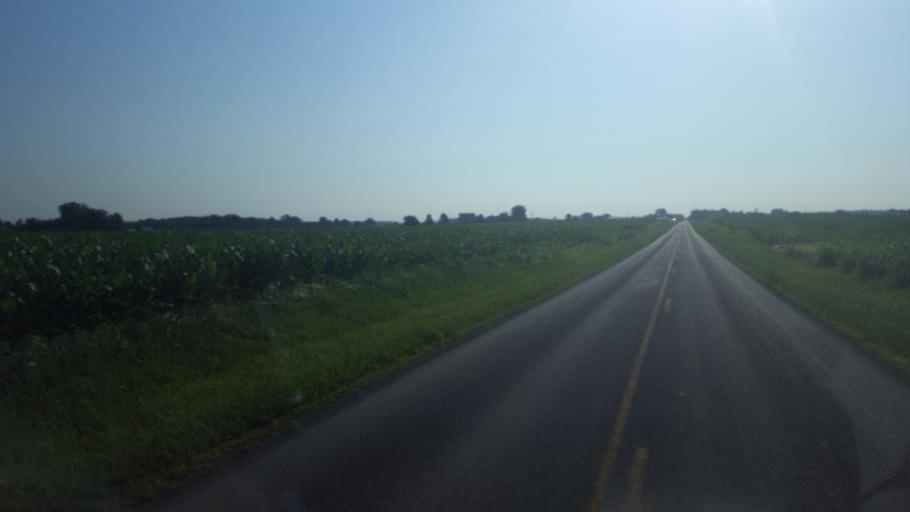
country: US
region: Ohio
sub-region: Hardin County
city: Kenton
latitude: 40.5623
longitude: -83.5505
